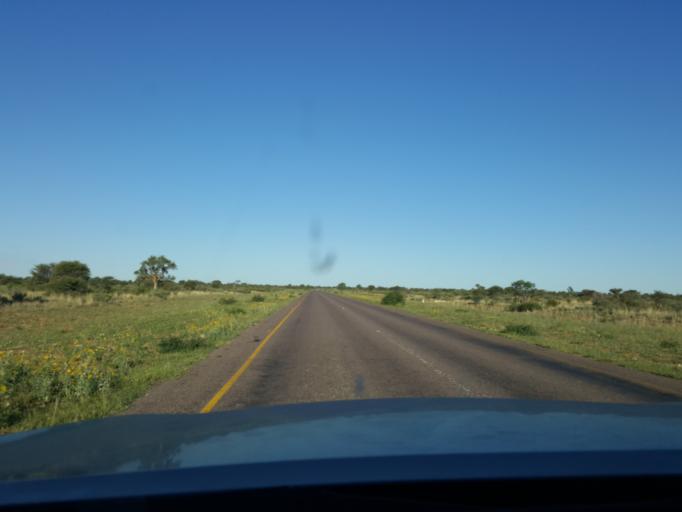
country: BW
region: Southern
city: Khakhea
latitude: -24.3008
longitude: 23.3898
